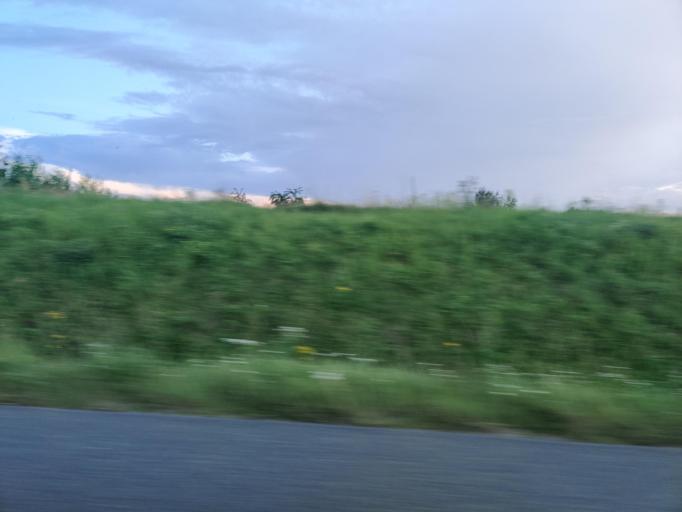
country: PL
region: Greater Poland Voivodeship
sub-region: Konin
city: Konin
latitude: 52.1953
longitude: 18.3102
